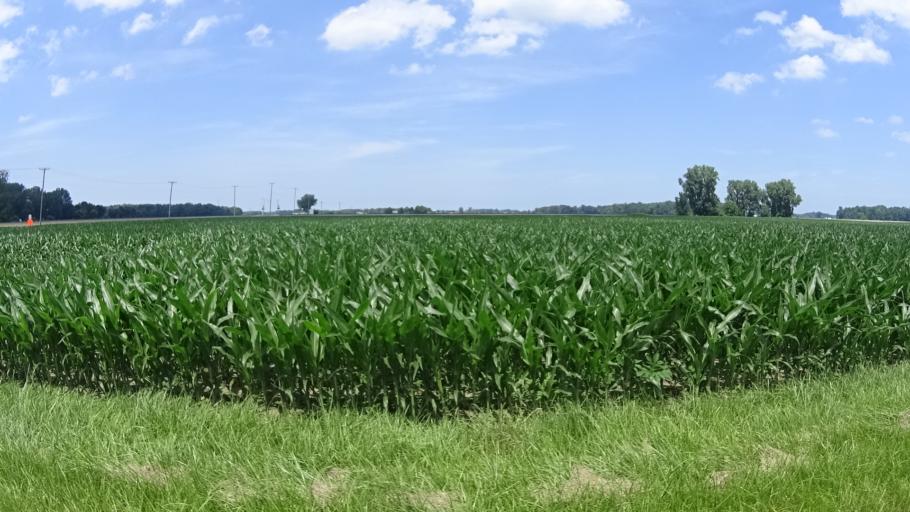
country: US
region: Ohio
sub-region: Erie County
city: Huron
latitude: 41.3405
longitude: -82.5354
